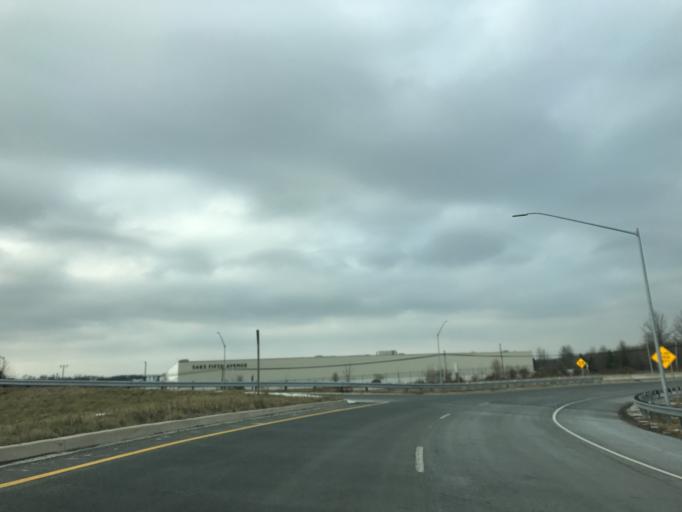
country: US
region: Maryland
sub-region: Harford County
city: Aberdeen
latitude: 39.4936
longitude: -76.1822
